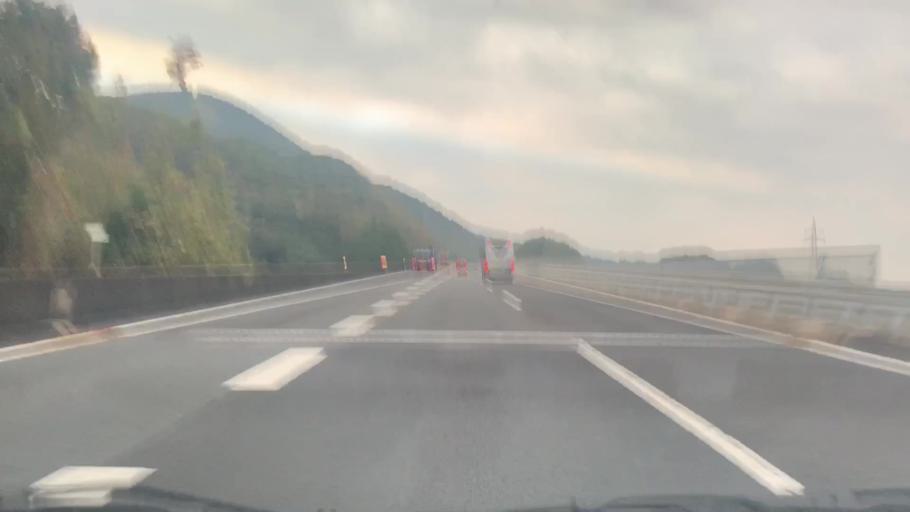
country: JP
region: Nagasaki
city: Omura
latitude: 32.9918
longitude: 129.9544
